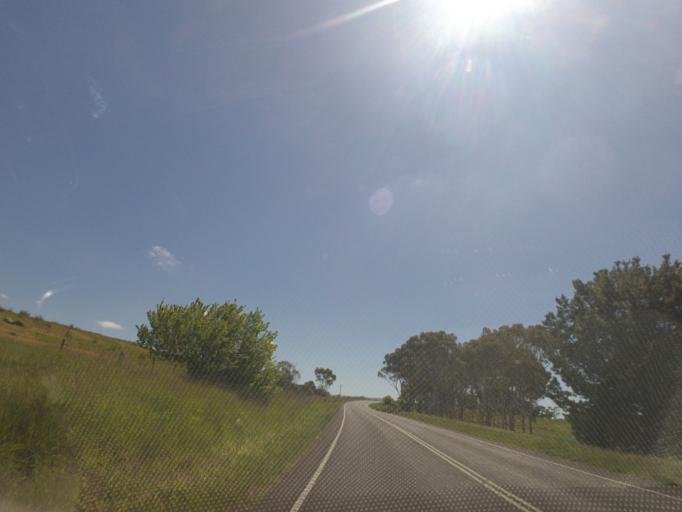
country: AU
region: Victoria
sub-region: Hume
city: Sunbury
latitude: -37.4648
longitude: 144.7437
